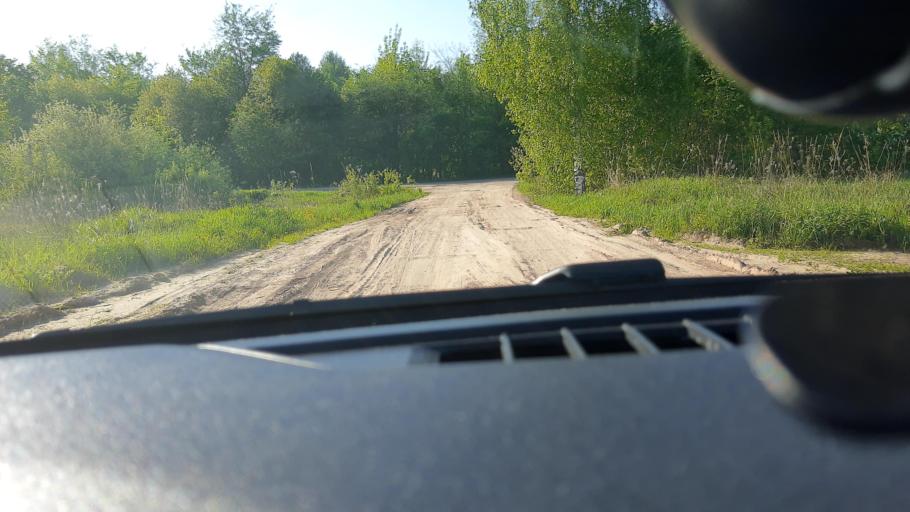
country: RU
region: Nizjnij Novgorod
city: Burevestnik
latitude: 56.1760
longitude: 43.8990
